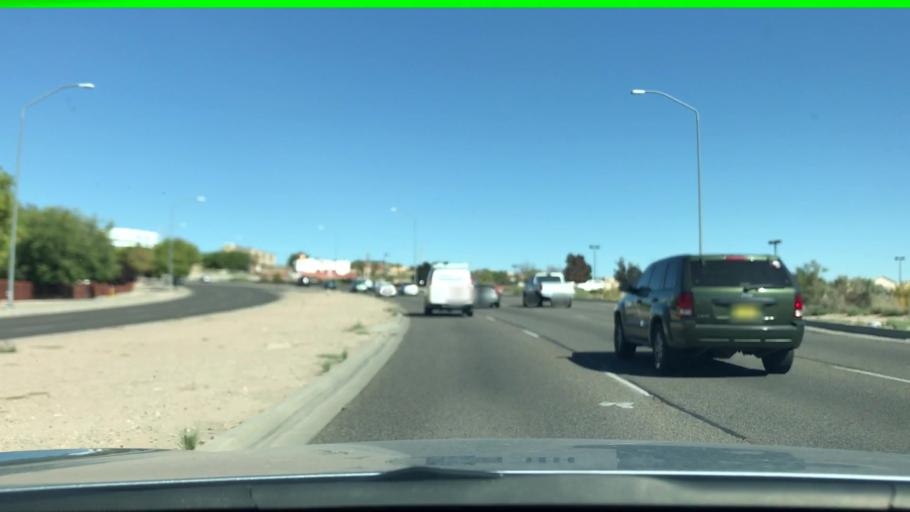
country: US
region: New Mexico
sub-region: Sandoval County
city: Rio Rancho
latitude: 35.2078
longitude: -106.6585
